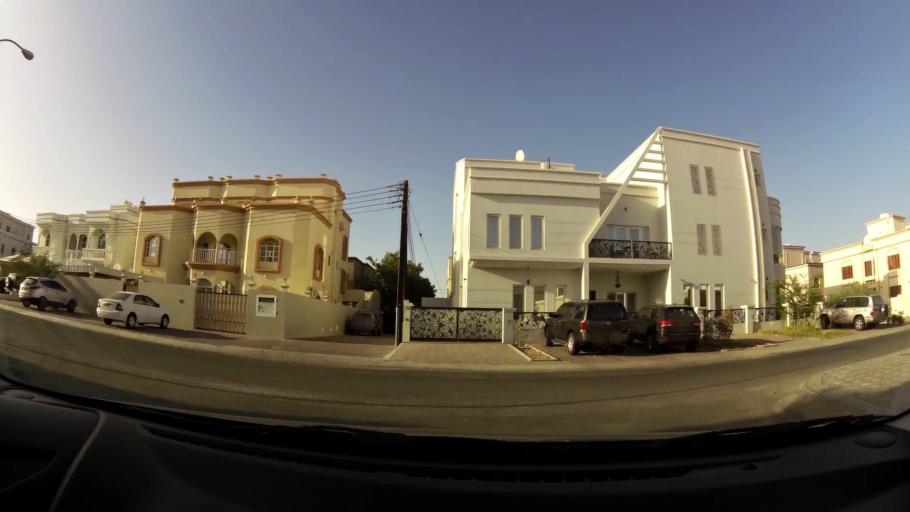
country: OM
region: Muhafazat Masqat
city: As Sib al Jadidah
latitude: 23.6131
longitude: 58.2204
